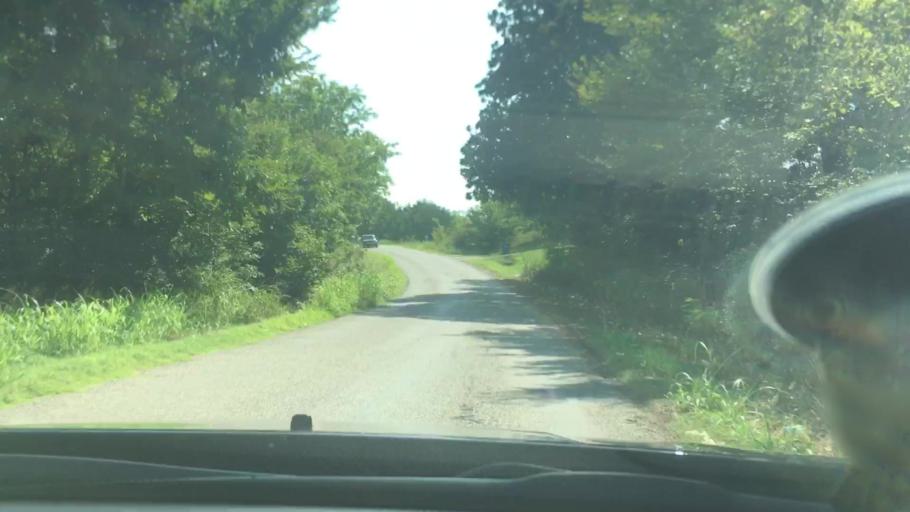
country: US
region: Oklahoma
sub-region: Bryan County
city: Colbert
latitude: 33.9110
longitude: -96.5189
